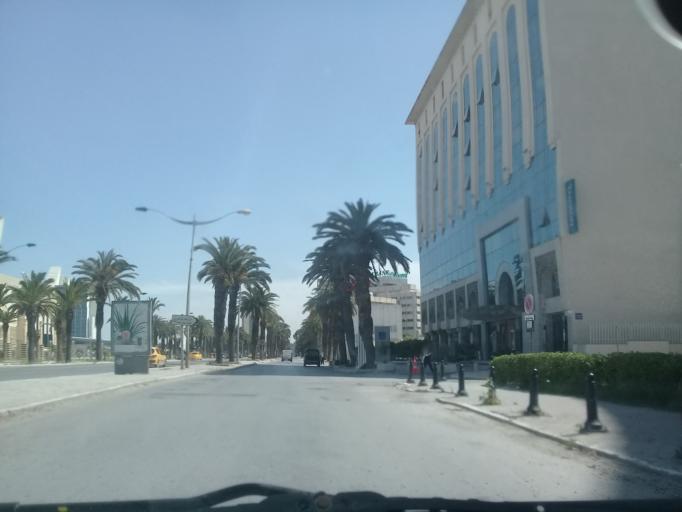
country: TN
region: Tunis
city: Tunis
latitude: 36.8120
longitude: 10.1843
